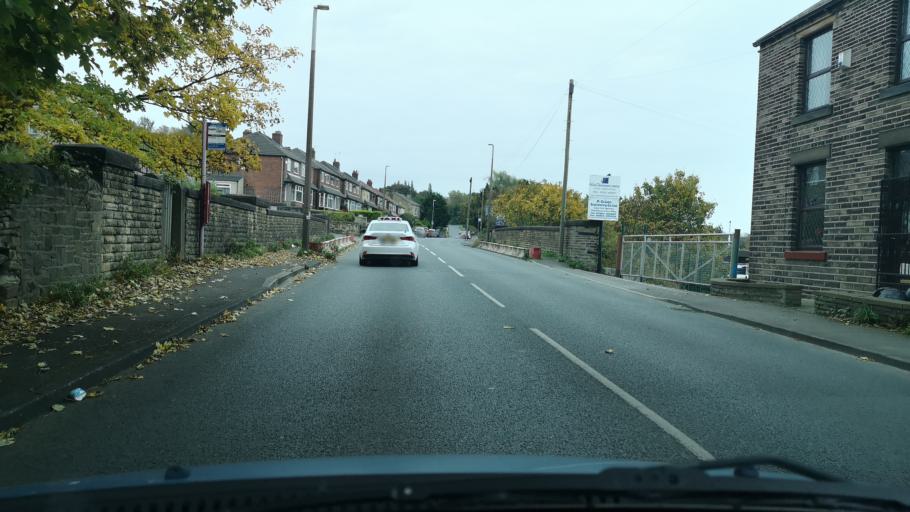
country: GB
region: England
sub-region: Kirklees
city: Heckmondwike
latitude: 53.7026
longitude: -1.6686
